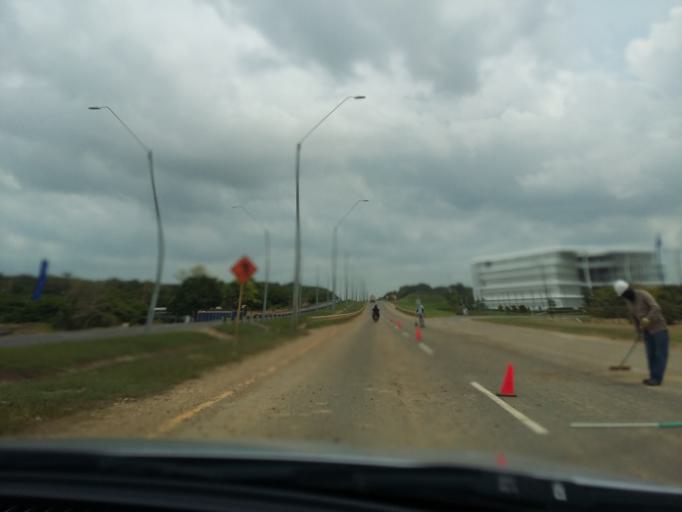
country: CO
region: Bolivar
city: Cartagena
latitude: 10.5057
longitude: -75.4732
